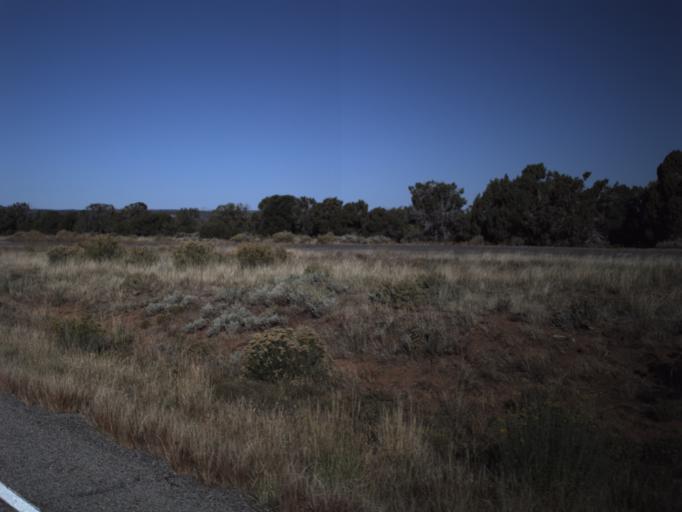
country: US
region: Utah
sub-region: San Juan County
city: Blanding
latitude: 37.5407
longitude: -109.9616
